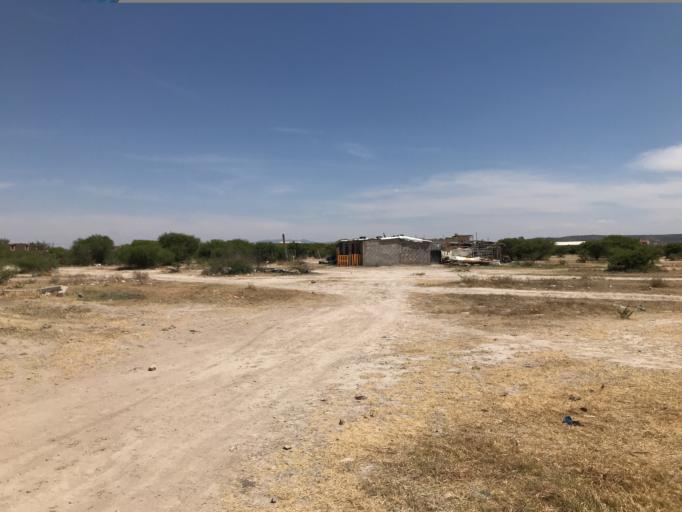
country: MX
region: Durango
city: Victoria de Durango
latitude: 23.9829
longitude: -104.6853
